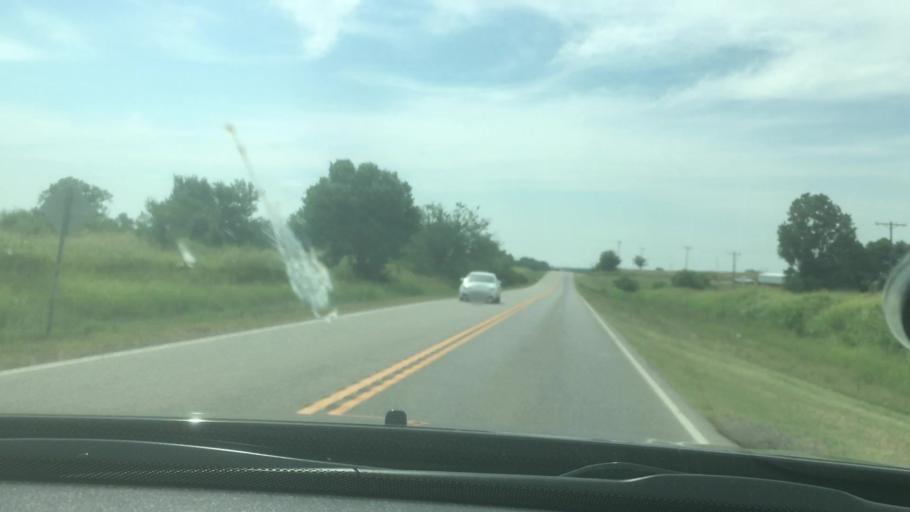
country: US
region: Oklahoma
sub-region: Garvin County
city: Maysville
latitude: 34.8102
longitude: -97.3771
